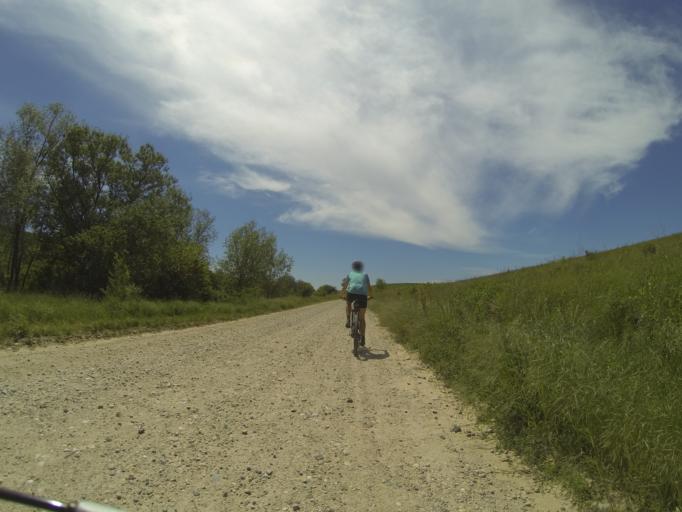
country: RO
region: Dolj
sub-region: Comuna Teslui
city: Teslui
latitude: 44.2009
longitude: 24.1347
